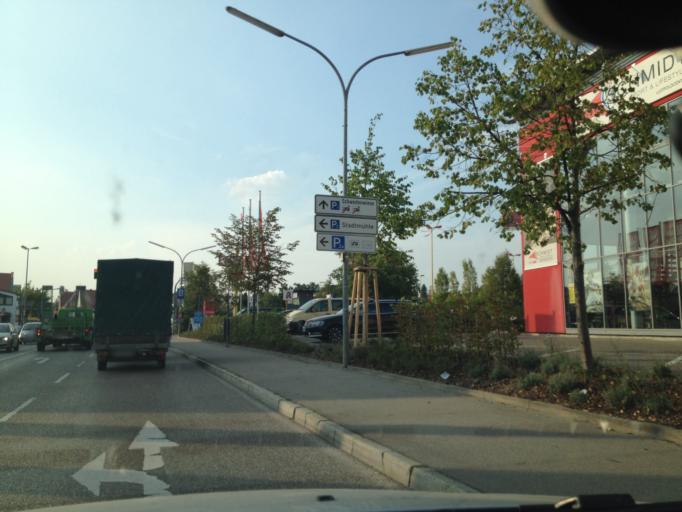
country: DE
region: Bavaria
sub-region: Regierungsbezirk Mittelfranken
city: Dinkelsbuhl
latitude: 49.0670
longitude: 10.3295
